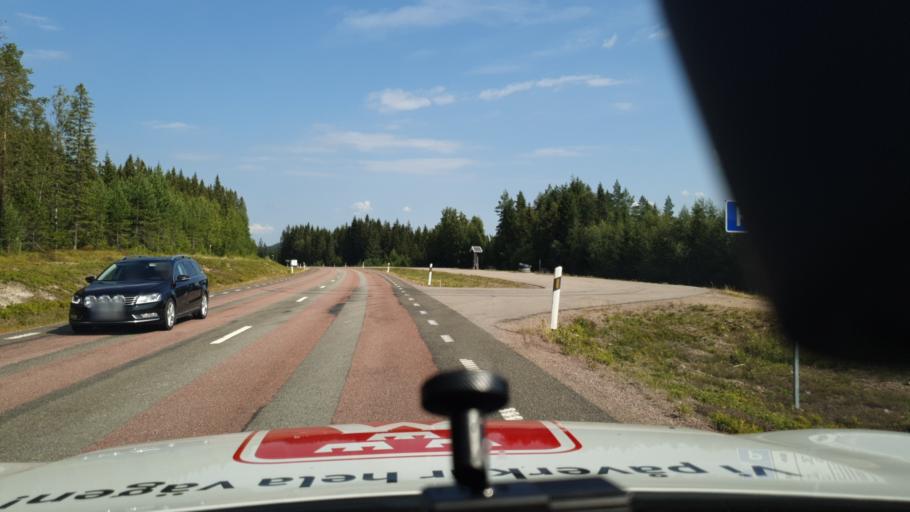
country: SE
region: Dalarna
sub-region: Malung-Saelens kommun
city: Malung
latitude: 60.5719
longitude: 13.5747
